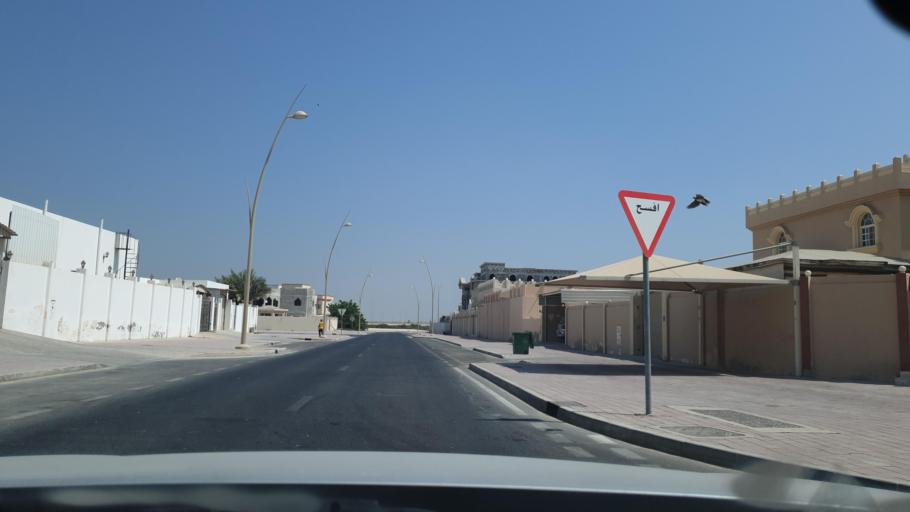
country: QA
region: Al Khawr
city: Al Khawr
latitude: 25.6827
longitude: 51.5234
